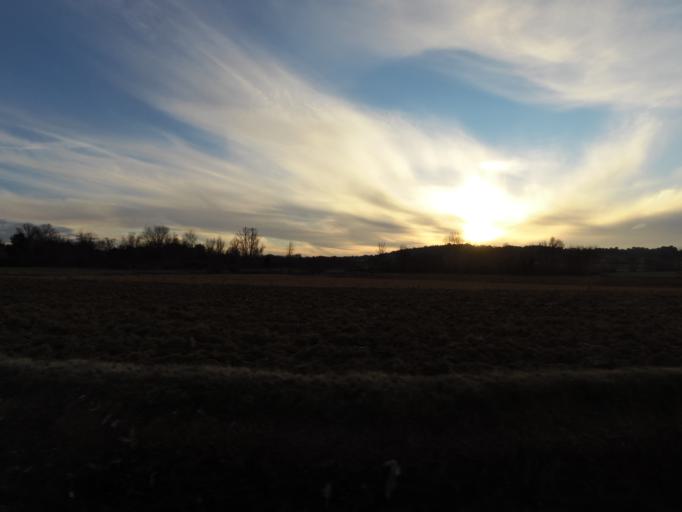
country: FR
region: Languedoc-Roussillon
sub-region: Departement du Gard
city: Saint-Mamert-du-Gard
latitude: 43.8759
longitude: 4.2028
